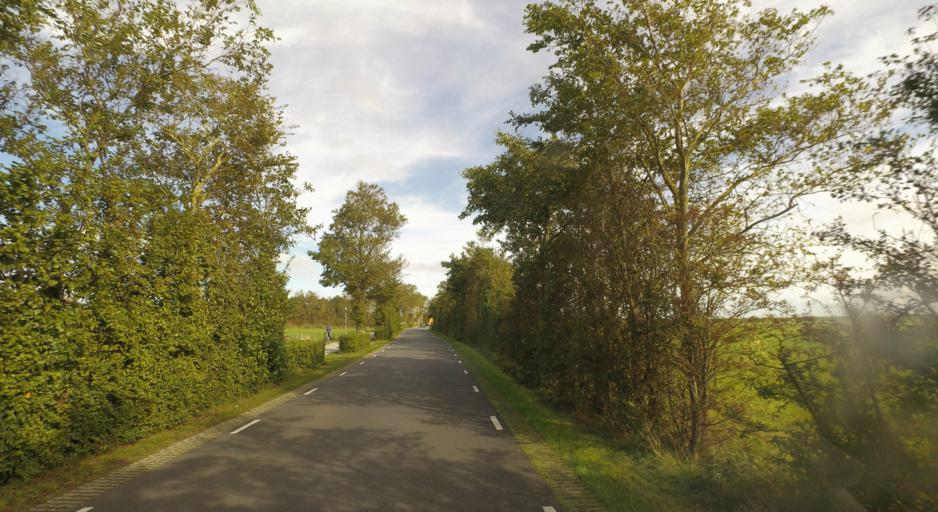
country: NL
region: Friesland
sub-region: Gemeente Ameland
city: Nes
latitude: 53.4472
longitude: 5.7848
